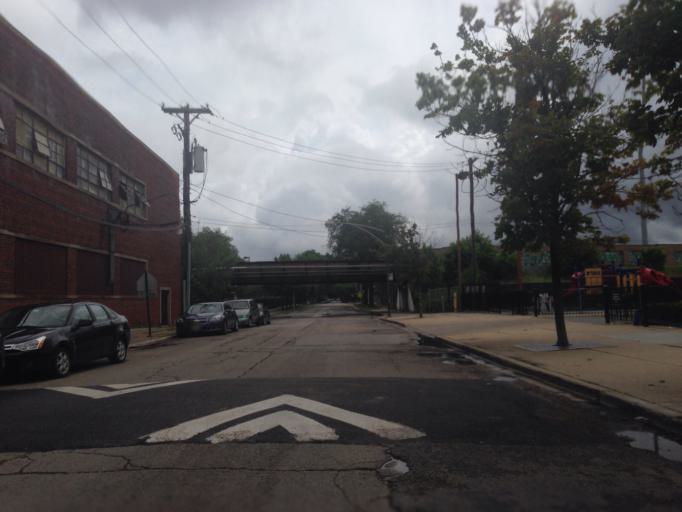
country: US
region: Illinois
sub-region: Cook County
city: Oak Park
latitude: 41.9154
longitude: -87.7240
